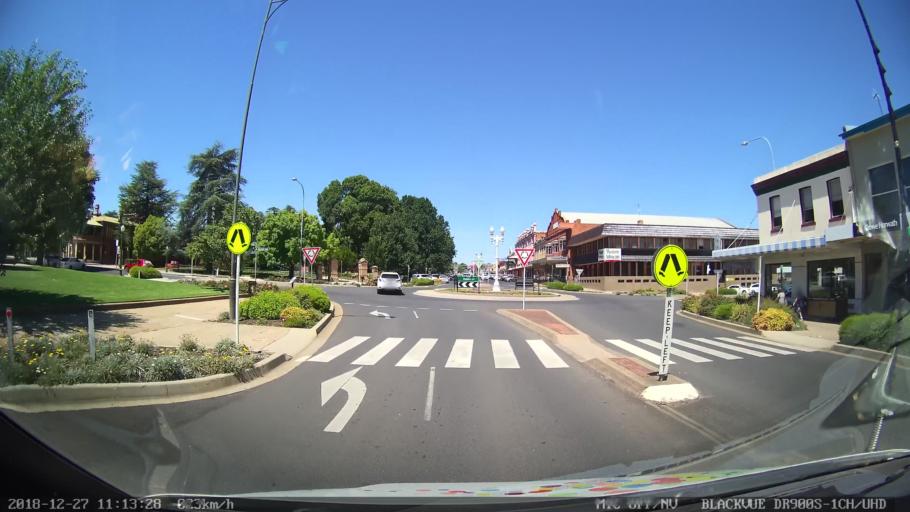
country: AU
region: New South Wales
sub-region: Bathurst Regional
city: Bathurst
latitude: -33.4167
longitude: 149.5786
